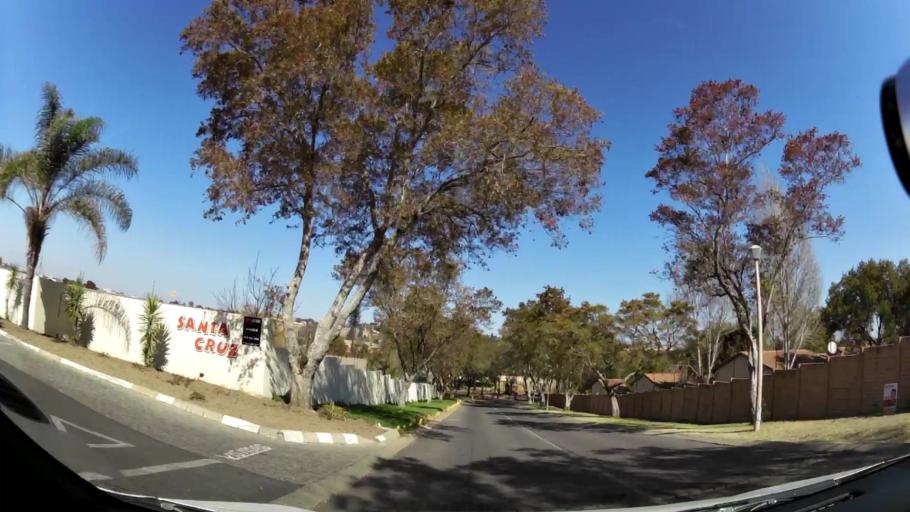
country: ZA
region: Gauteng
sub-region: City of Johannesburg Metropolitan Municipality
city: Midrand
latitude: -25.9455
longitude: 28.1256
